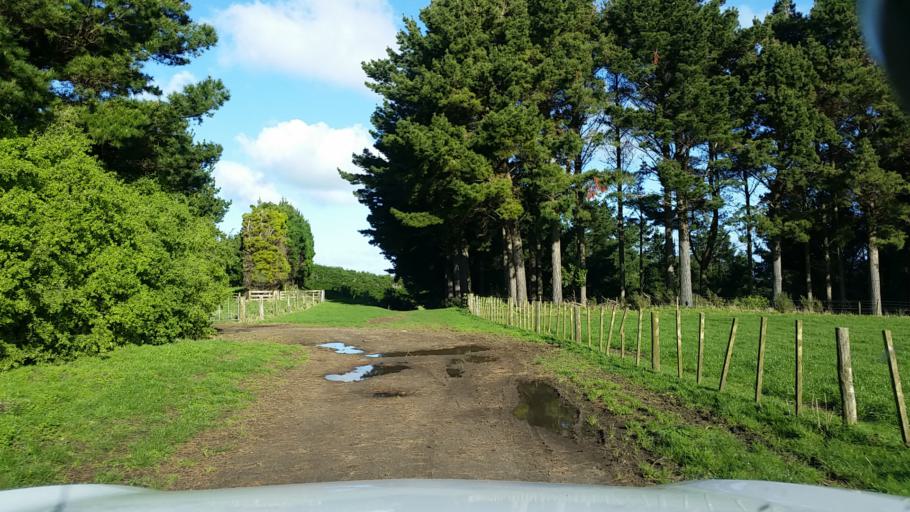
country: NZ
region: Taranaki
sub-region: South Taranaki District
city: Patea
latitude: -39.7421
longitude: 174.5437
